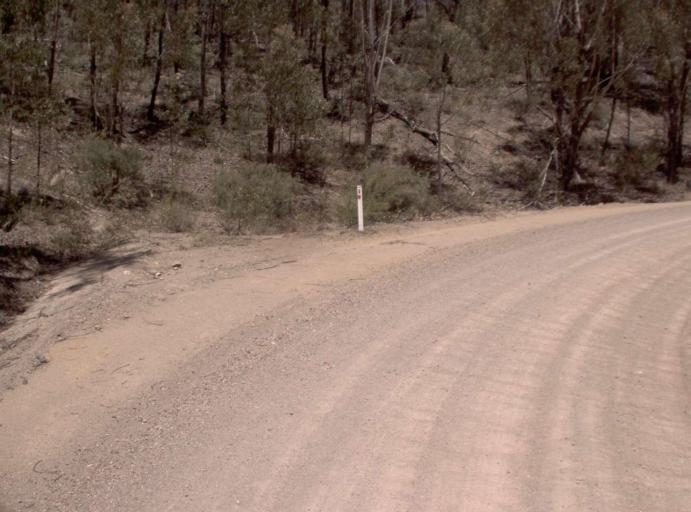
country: AU
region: New South Wales
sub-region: Snowy River
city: Jindabyne
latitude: -37.0807
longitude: 148.3296
